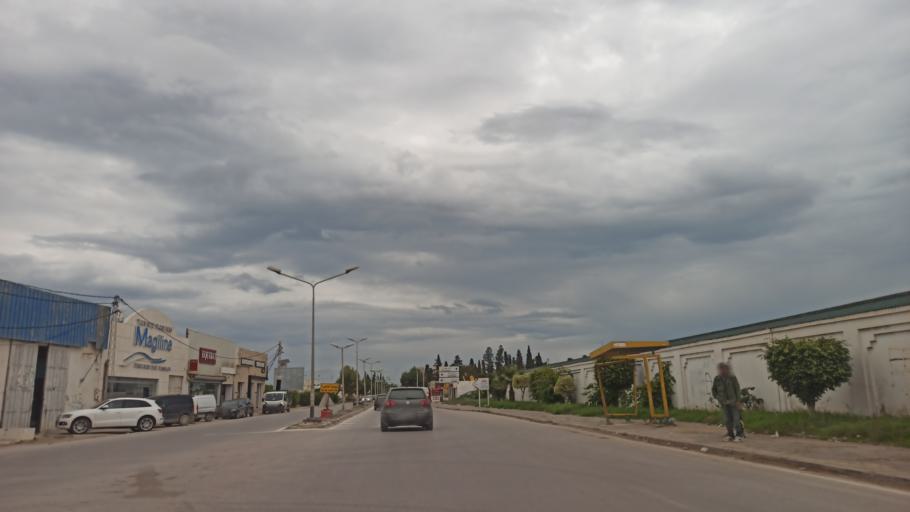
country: TN
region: Ariana
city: Ariana
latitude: 36.8708
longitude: 10.2317
